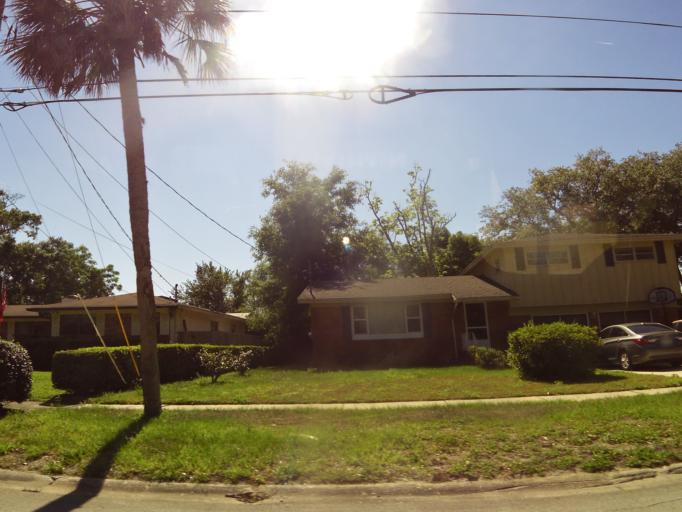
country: US
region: Florida
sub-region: Duval County
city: Jacksonville
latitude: 30.3396
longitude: -81.5685
